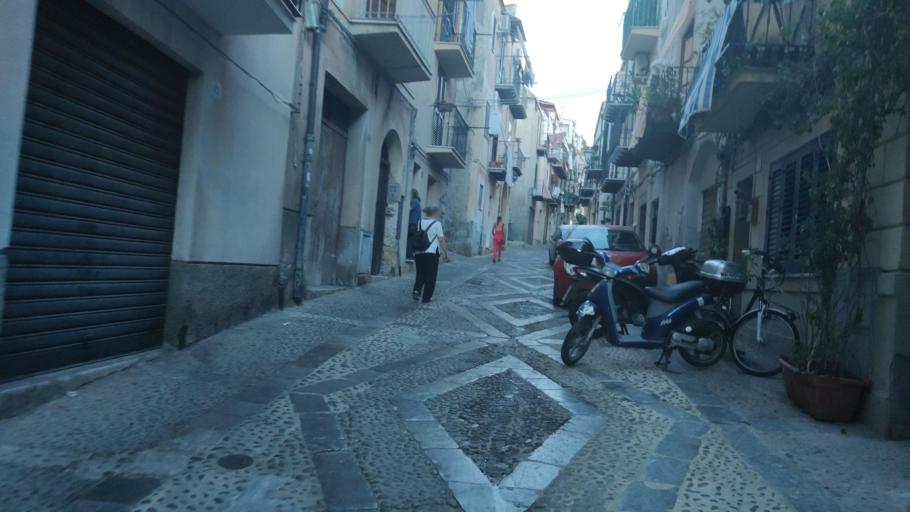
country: IT
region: Sicily
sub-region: Palermo
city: Cefalu
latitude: 38.0380
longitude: 14.0206
